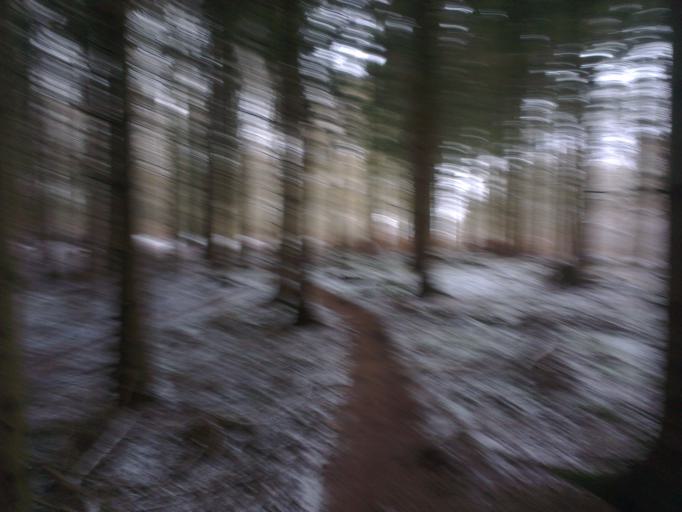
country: DK
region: Capital Region
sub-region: Frederikssund Kommune
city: Frederikssund
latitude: 55.8491
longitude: 12.0254
